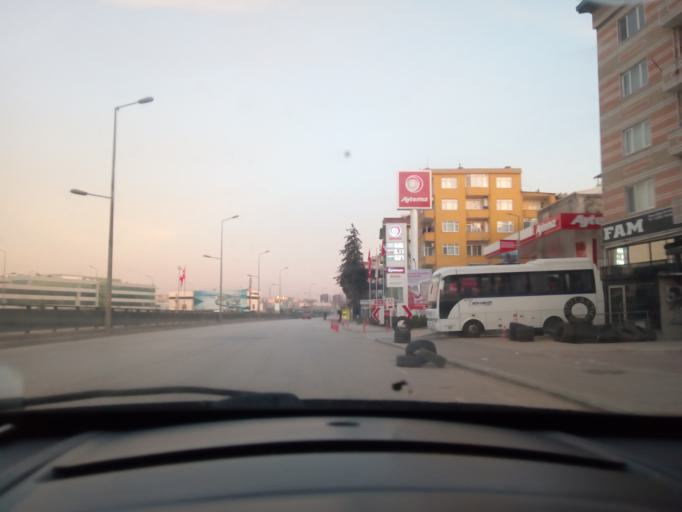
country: TR
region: Bursa
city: Niluefer
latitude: 40.2523
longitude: 28.9558
